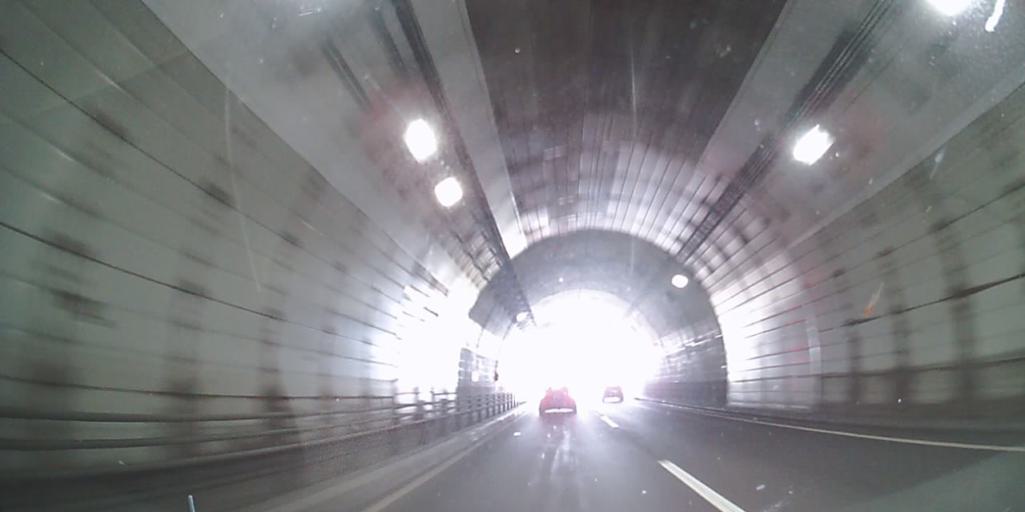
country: JP
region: Hokkaido
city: Muroran
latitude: 42.3416
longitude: 141.0312
